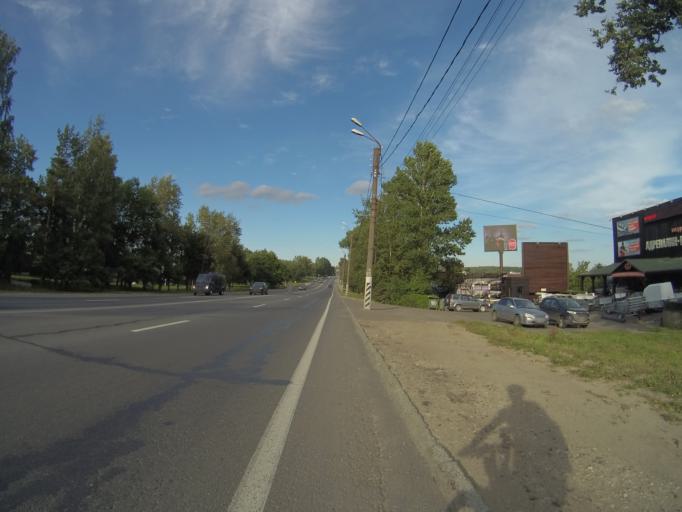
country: RU
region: Vladimir
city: Raduzhnyy
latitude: 56.0971
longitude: 40.2594
